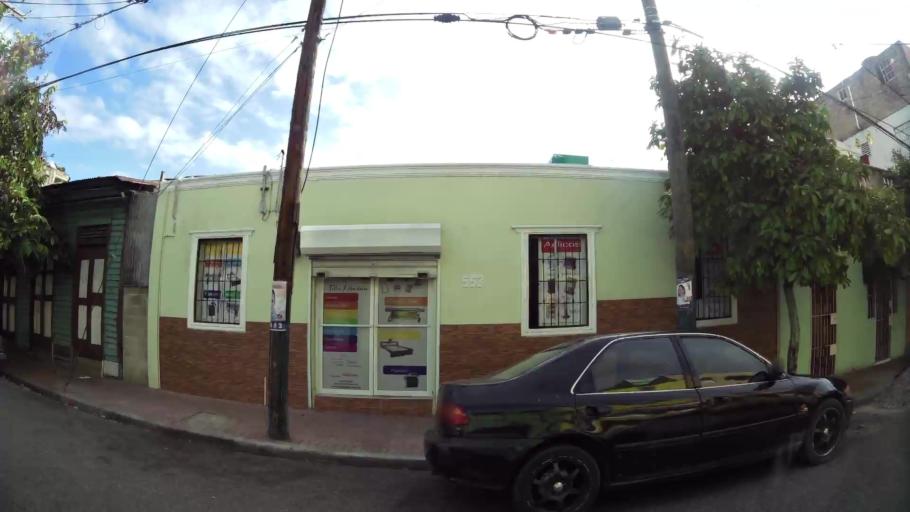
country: DO
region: Nacional
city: San Carlos
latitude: 18.4779
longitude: -69.8895
